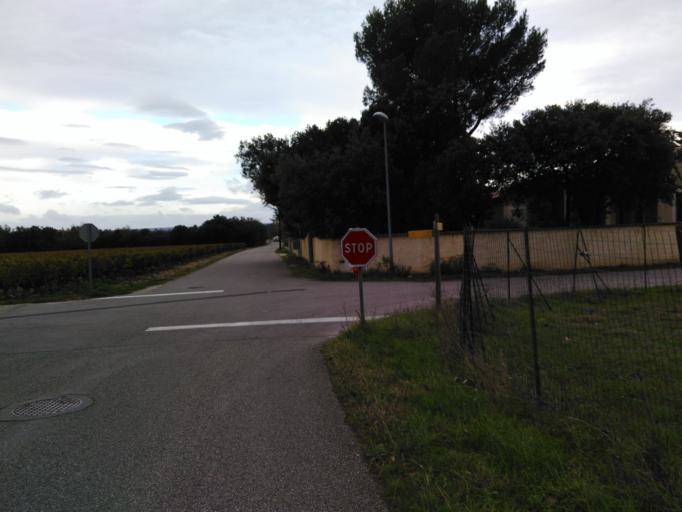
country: FR
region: Provence-Alpes-Cote d'Azur
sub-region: Departement du Vaucluse
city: Grillon
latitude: 44.3861
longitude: 4.9303
